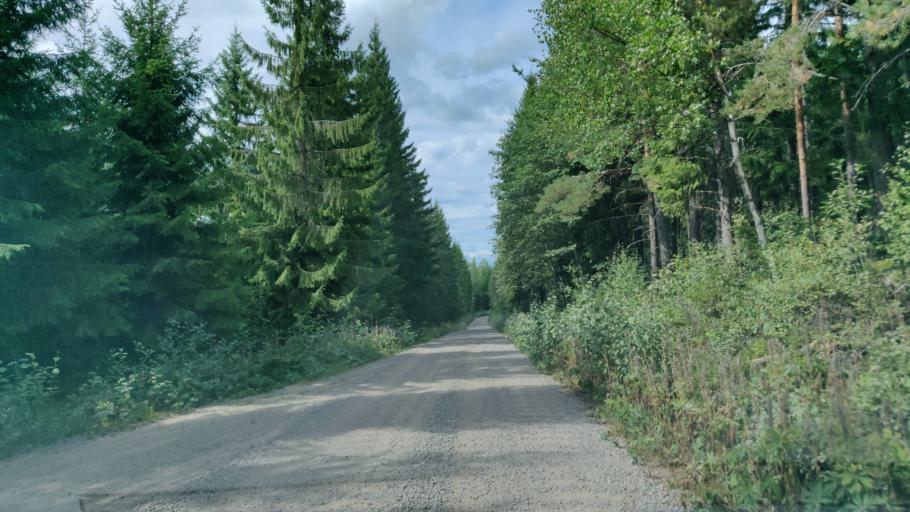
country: SE
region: Vaermland
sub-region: Hagfors Kommun
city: Hagfors
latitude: 60.0075
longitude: 13.7122
